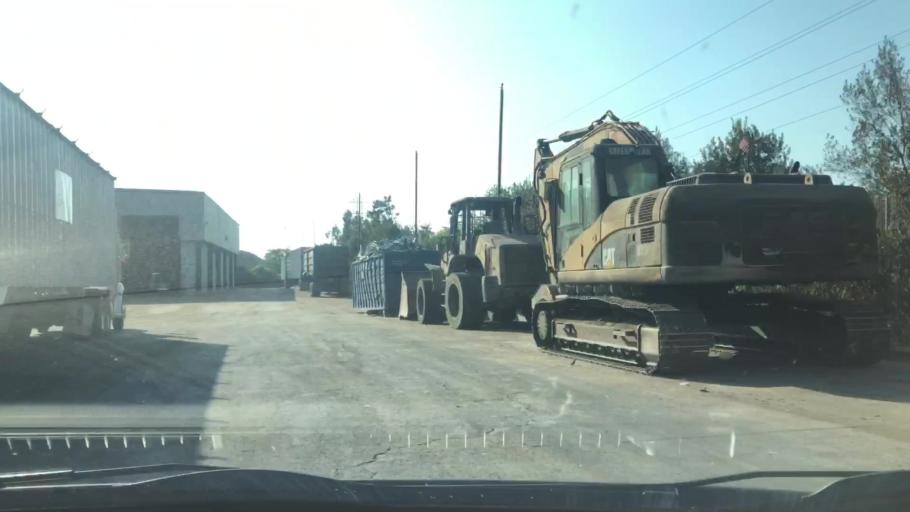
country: US
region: California
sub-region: Santa Clara County
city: Sunnyvale
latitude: 37.4186
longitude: -122.0104
